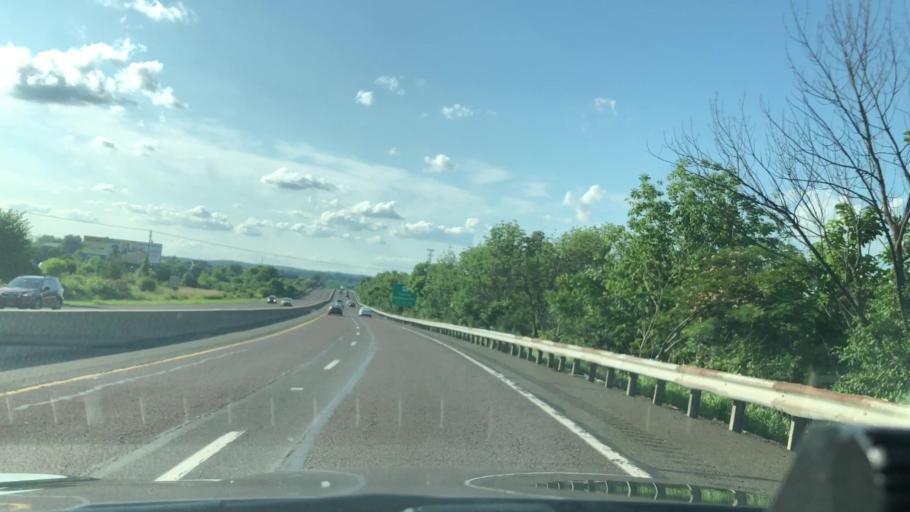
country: US
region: Pennsylvania
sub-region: Bucks County
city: Sellersville
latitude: 40.3344
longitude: -75.3105
